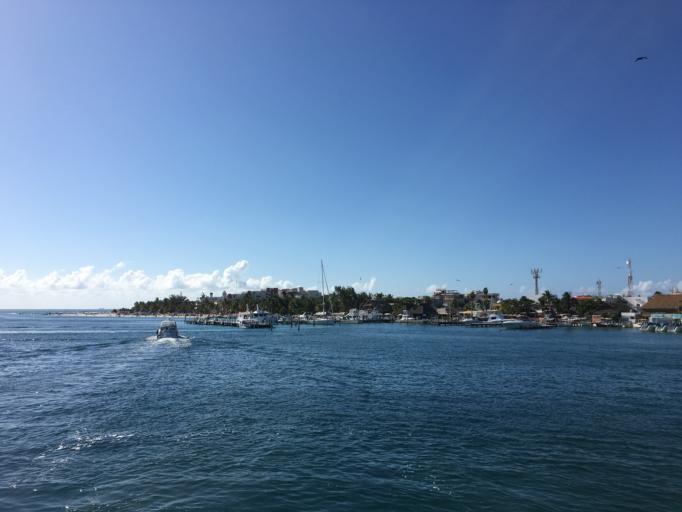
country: MX
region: Quintana Roo
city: Isla Mujeres
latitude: 21.2535
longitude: -86.7476
